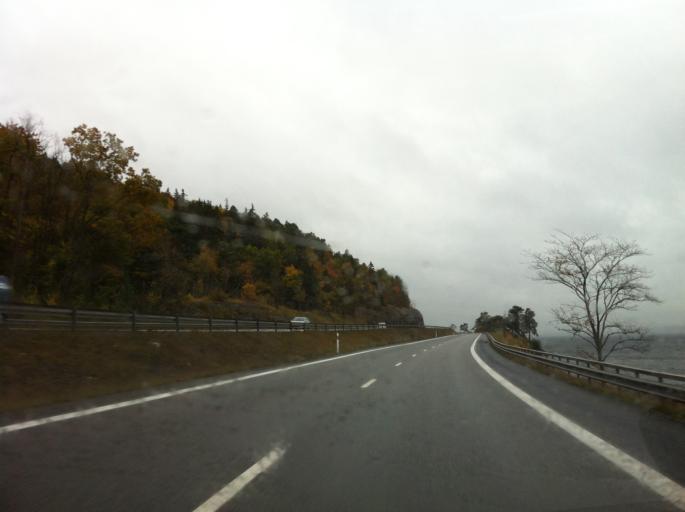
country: SE
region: Joenkoeping
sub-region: Jonkopings Kommun
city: Kaxholmen
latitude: 57.8681
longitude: 14.2709
